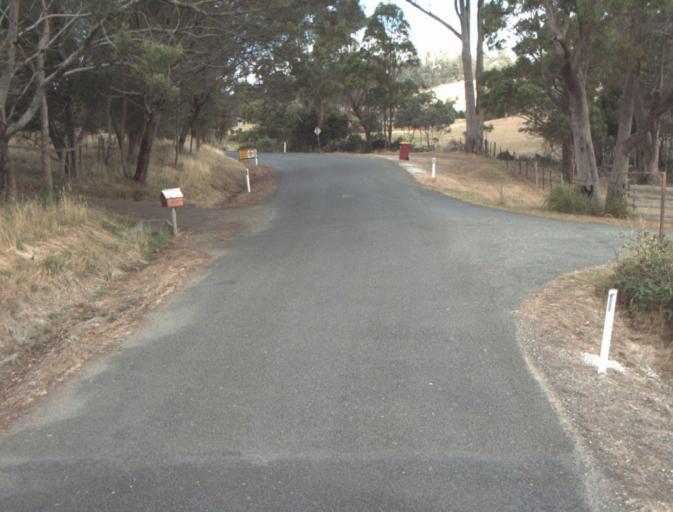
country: AU
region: Tasmania
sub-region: Launceston
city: Mayfield
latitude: -41.2973
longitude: 147.0301
